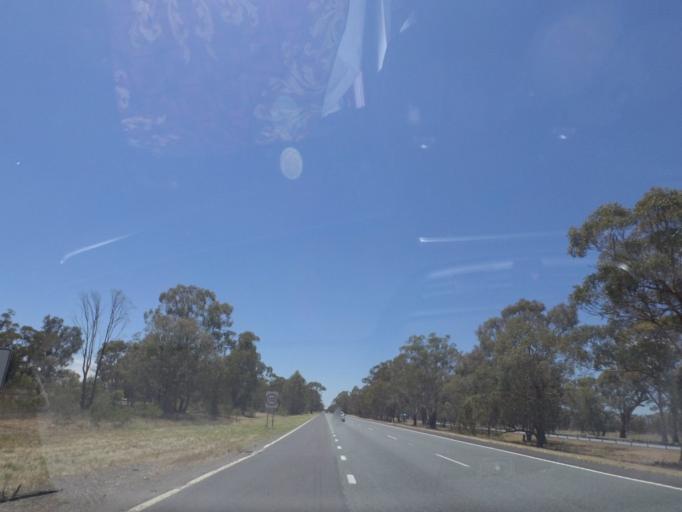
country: AU
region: Victoria
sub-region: Benalla
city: Benalla
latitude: -36.6186
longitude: 145.7758
